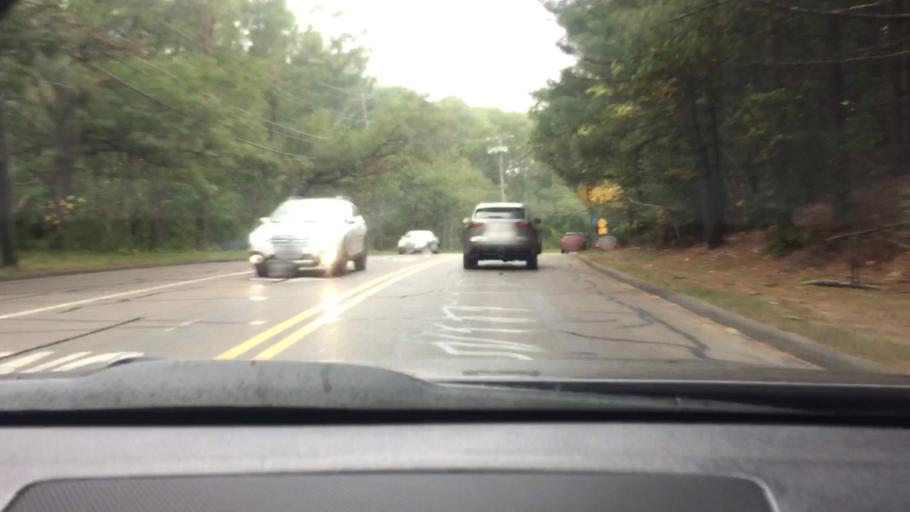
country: US
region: Massachusetts
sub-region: Norfolk County
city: Needham
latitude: 42.2969
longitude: -71.2017
